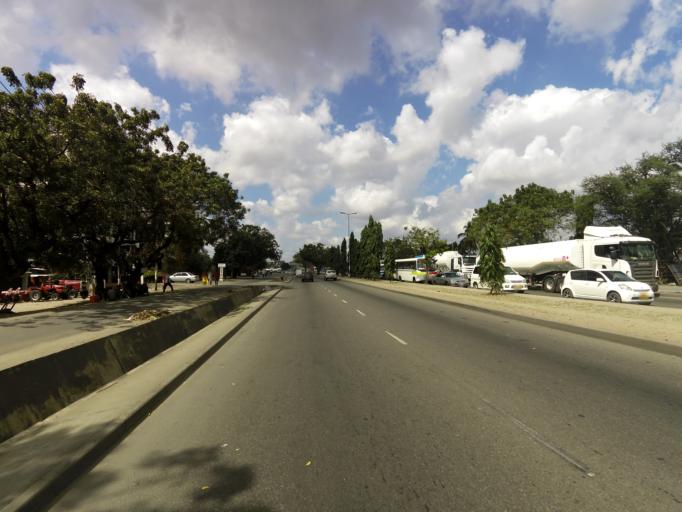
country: TZ
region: Dar es Salaam
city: Magomeni
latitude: -6.7974
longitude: 39.2069
